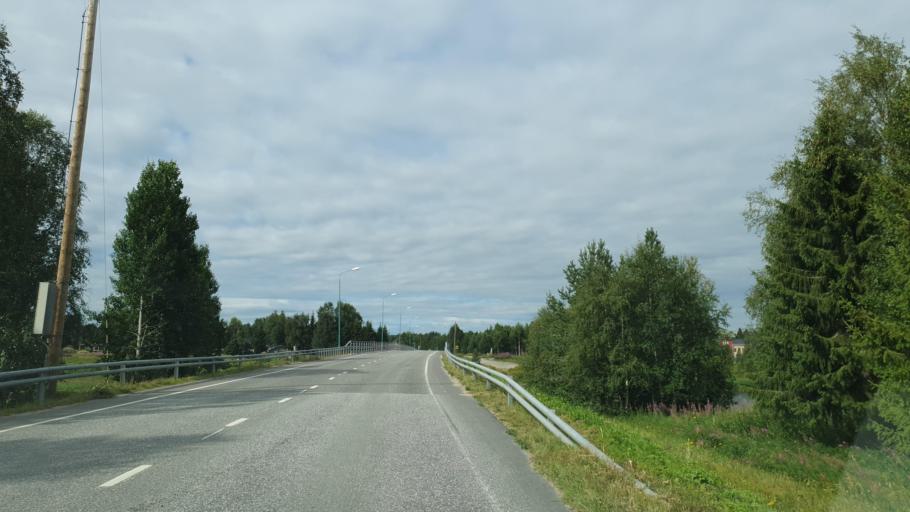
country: FI
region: Lapland
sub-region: Tunturi-Lappi
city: Kittilae
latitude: 67.6468
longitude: 24.9334
